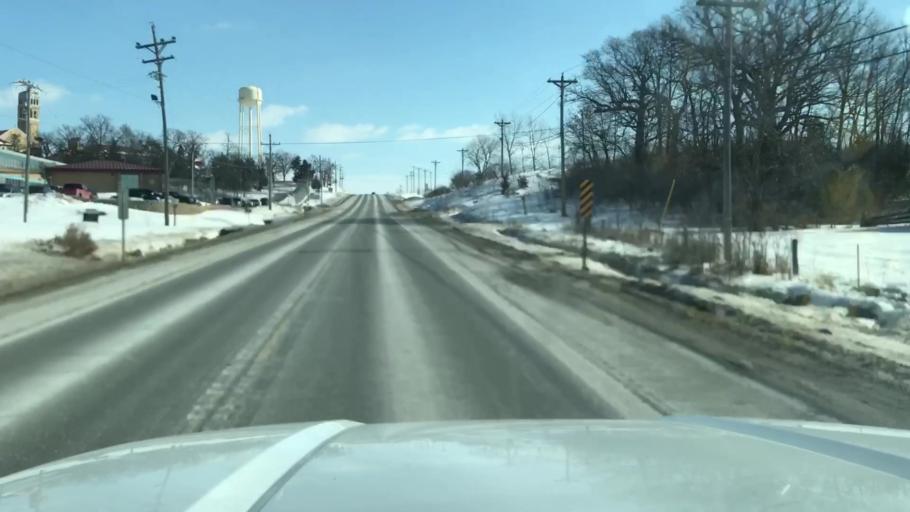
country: US
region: Missouri
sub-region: Nodaway County
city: Maryville
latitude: 40.3448
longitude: -94.8173
